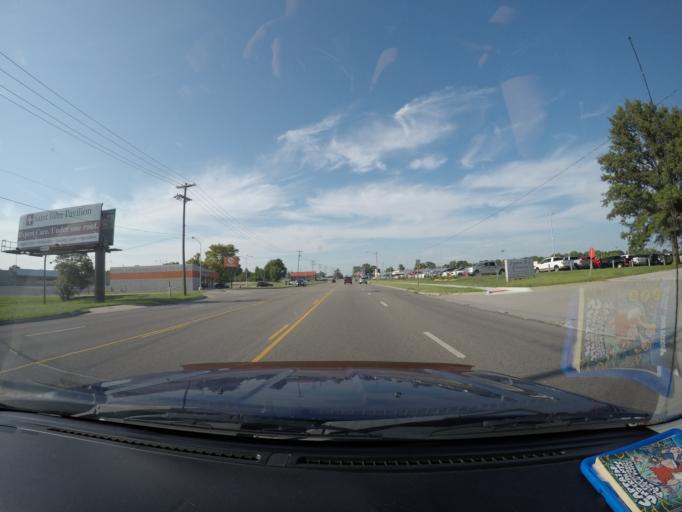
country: US
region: Kansas
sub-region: Leavenworth County
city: Lansing
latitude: 39.2705
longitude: -94.8998
